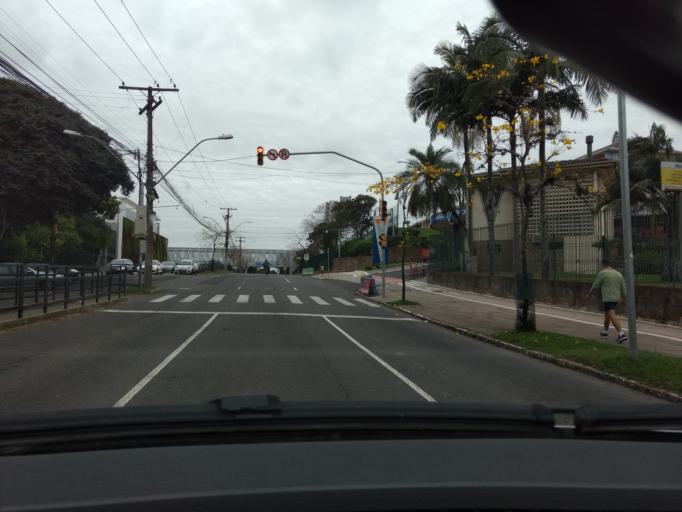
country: BR
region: Rio Grande do Sul
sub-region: Porto Alegre
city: Porto Alegre
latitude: -30.0285
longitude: -51.1772
